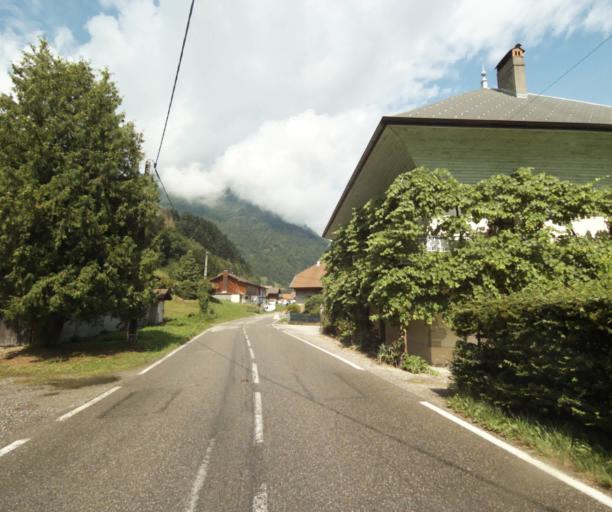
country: FR
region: Rhone-Alpes
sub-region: Departement de la Haute-Savoie
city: Thones
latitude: 45.8839
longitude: 6.3137
